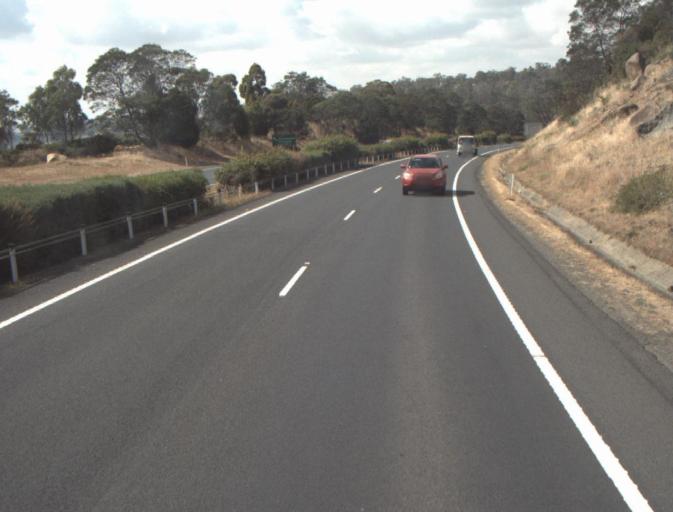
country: AU
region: Tasmania
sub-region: Launceston
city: Summerhill
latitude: -41.4800
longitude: 147.1489
